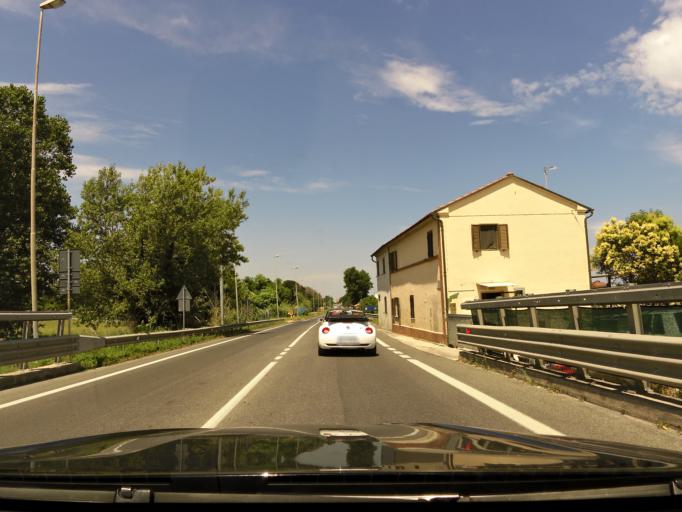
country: IT
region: The Marches
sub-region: Provincia di Pesaro e Urbino
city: Marotta
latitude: 43.7492
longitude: 13.1686
